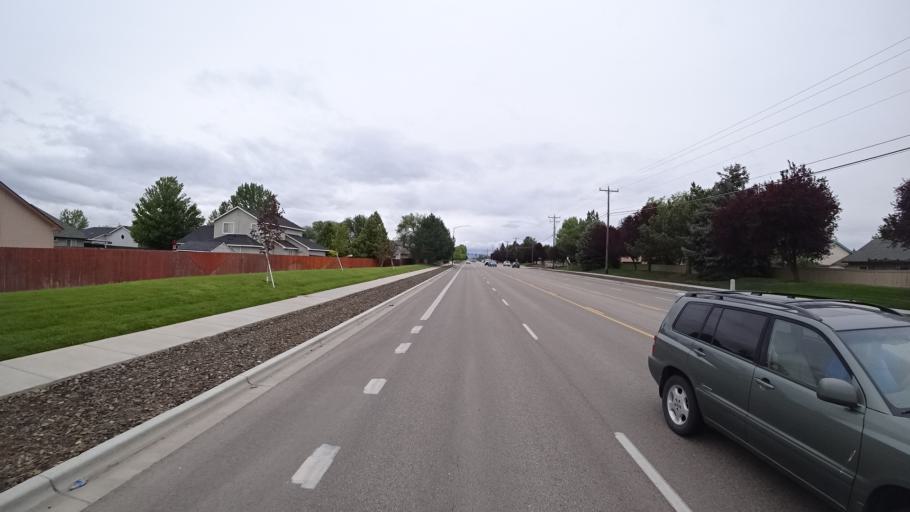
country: US
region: Idaho
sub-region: Ada County
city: Meridian
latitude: 43.6339
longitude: -116.3787
